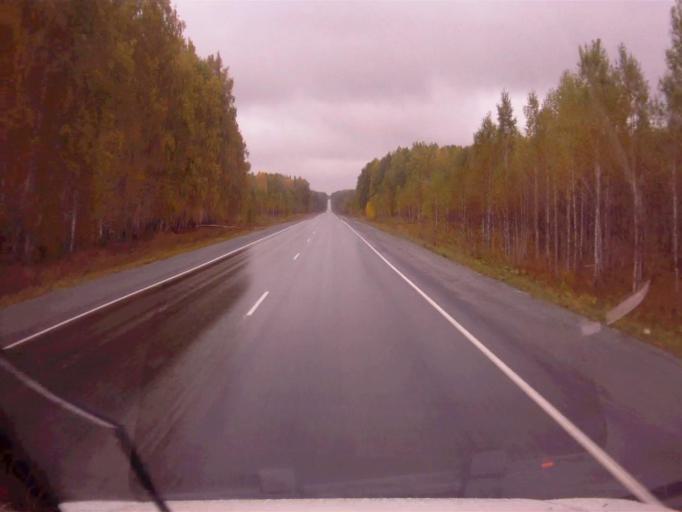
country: RU
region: Chelyabinsk
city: Tayginka
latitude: 55.5107
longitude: 60.6384
